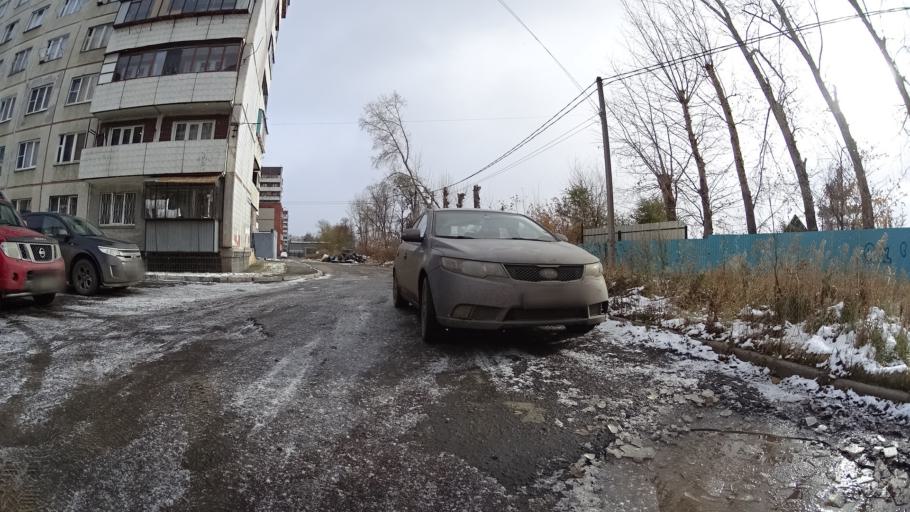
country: RU
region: Chelyabinsk
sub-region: Gorod Chelyabinsk
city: Chelyabinsk
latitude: 55.1878
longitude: 61.3124
